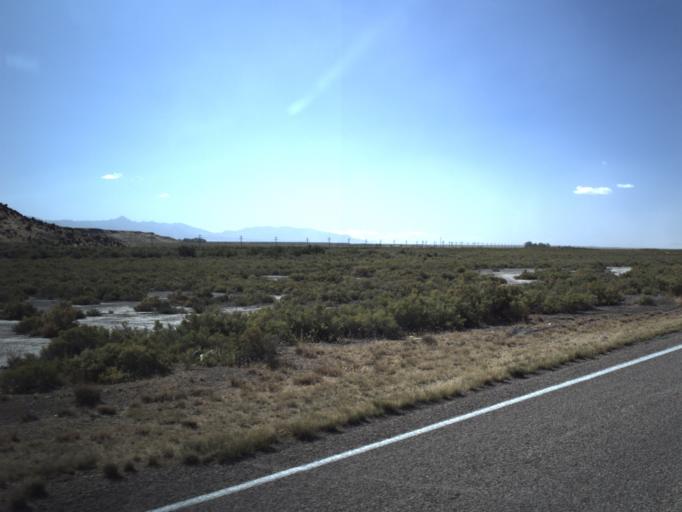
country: US
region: Utah
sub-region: Beaver County
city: Milford
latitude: 38.7349
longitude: -112.9646
